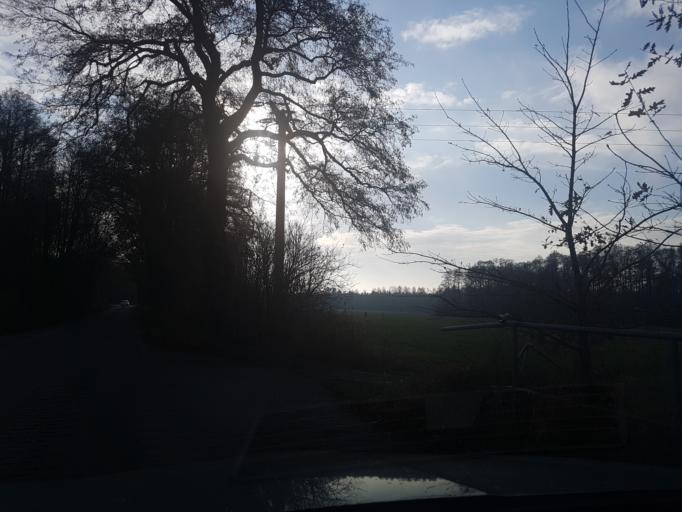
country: DE
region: Brandenburg
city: Ruckersdorf
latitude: 51.5493
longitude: 13.5975
